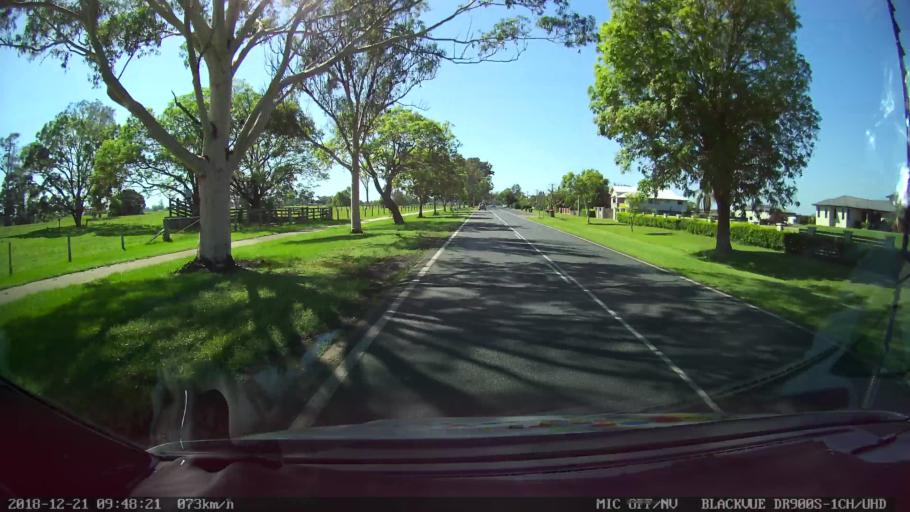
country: AU
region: New South Wales
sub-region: Clarence Valley
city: Grafton
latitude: -29.6522
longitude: 152.9329
